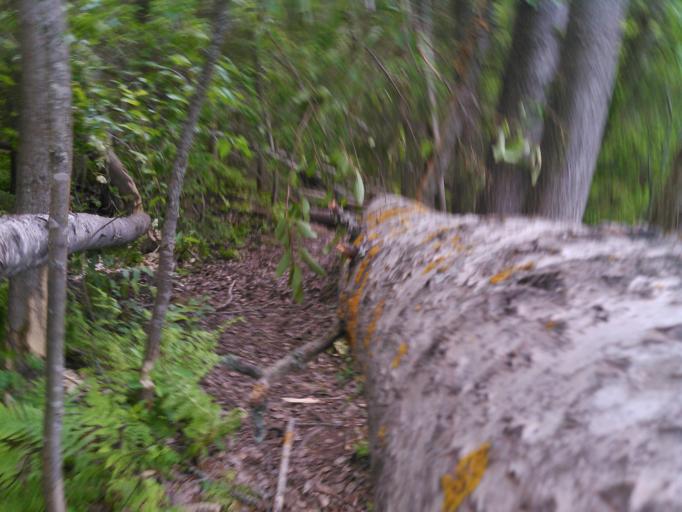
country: SE
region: Vaesterbotten
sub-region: Umea Kommun
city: Roback
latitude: 63.8235
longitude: 20.1998
